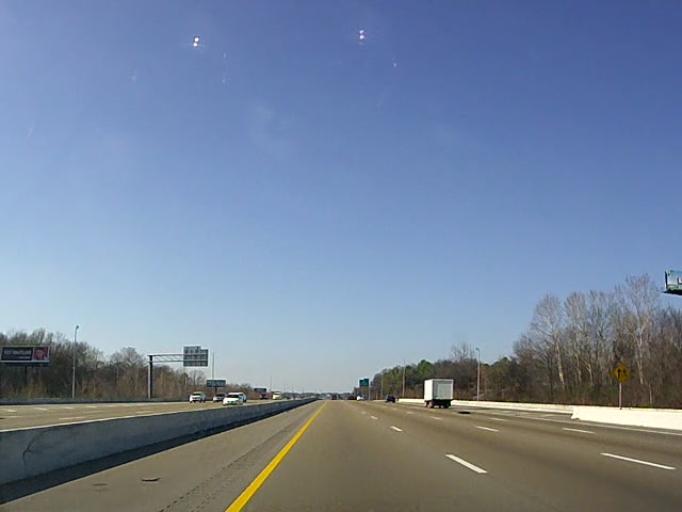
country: US
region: Mississippi
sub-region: De Soto County
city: Southaven
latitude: 35.0810
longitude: -89.9374
